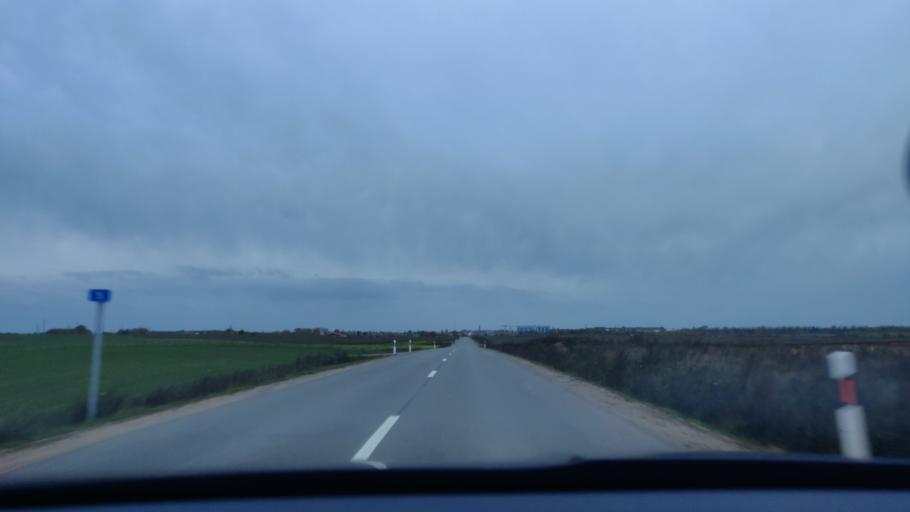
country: LT
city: Lentvaris
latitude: 54.6031
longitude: 25.0050
